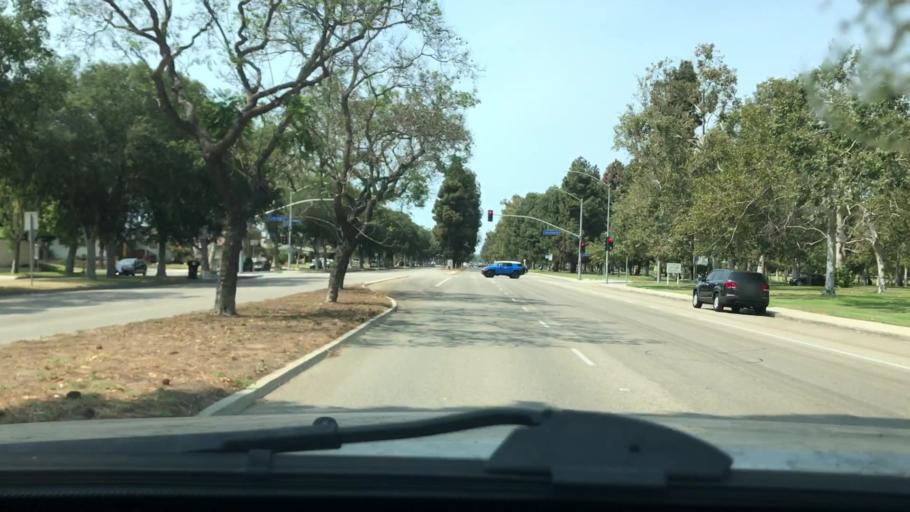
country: US
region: California
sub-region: Orange County
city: Rossmoor
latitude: 33.7988
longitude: -118.0991
